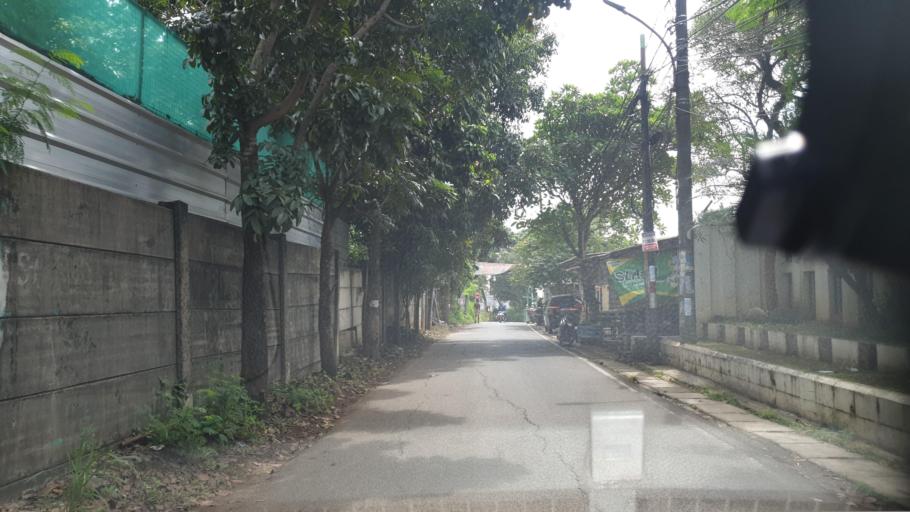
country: ID
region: West Java
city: Pamulang
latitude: -6.3479
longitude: 106.7710
